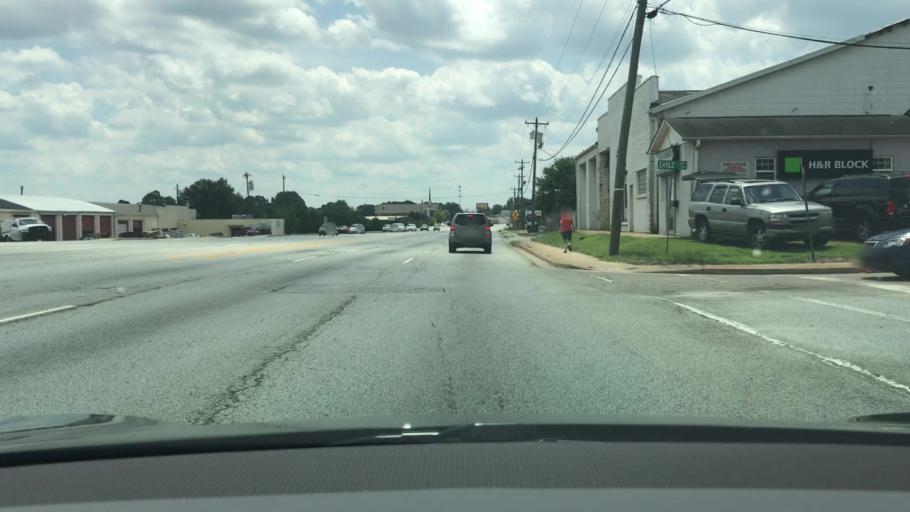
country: US
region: South Carolina
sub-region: Greenville County
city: Parker
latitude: 34.8453
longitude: -82.4462
